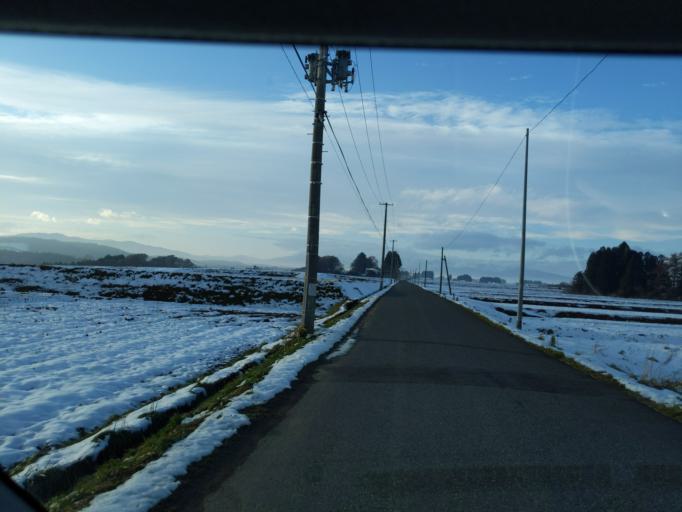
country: JP
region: Iwate
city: Mizusawa
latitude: 39.0478
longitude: 141.1066
